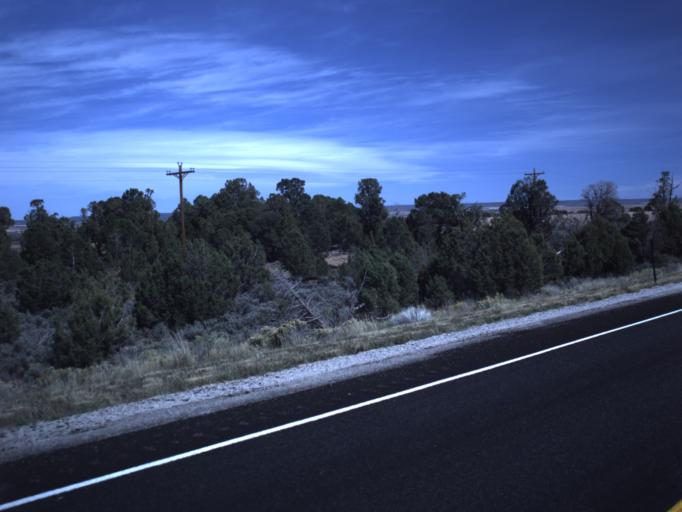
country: US
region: Colorado
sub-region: Dolores County
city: Dove Creek
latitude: 37.8282
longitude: -109.0828
